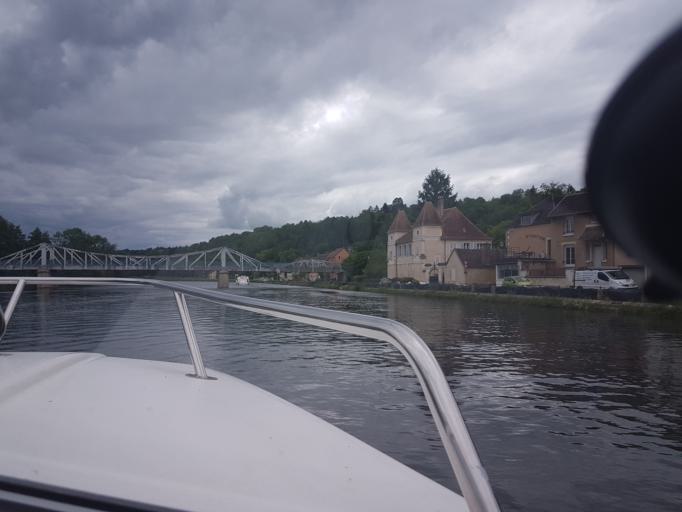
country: FR
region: Bourgogne
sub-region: Departement de l'Yonne
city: Augy
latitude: 47.7554
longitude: 3.5918
